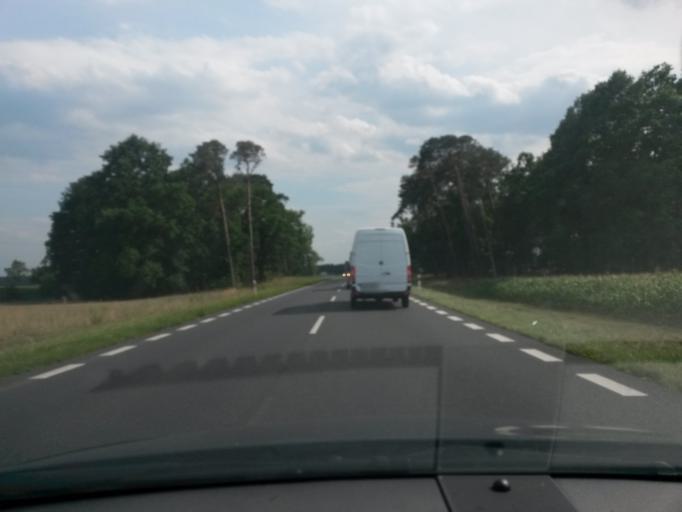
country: PL
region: Greater Poland Voivodeship
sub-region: Powiat sremski
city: Srem
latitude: 52.1239
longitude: 17.0438
